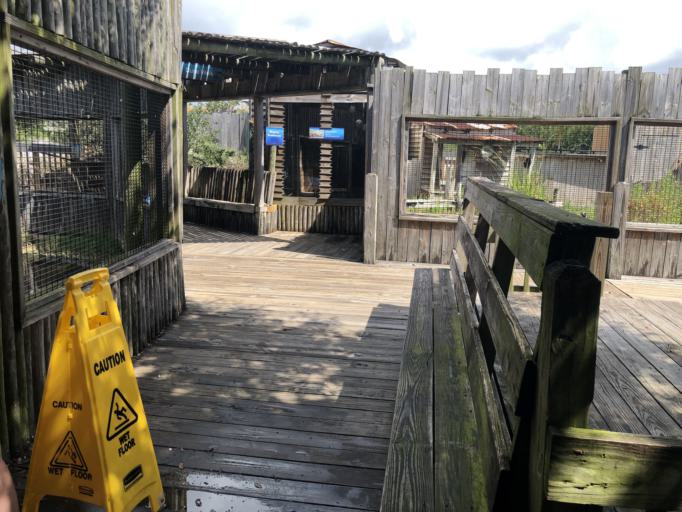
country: US
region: Florida
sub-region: Okaloosa County
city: Fort Walton Beach
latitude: 30.3946
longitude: -86.5946
